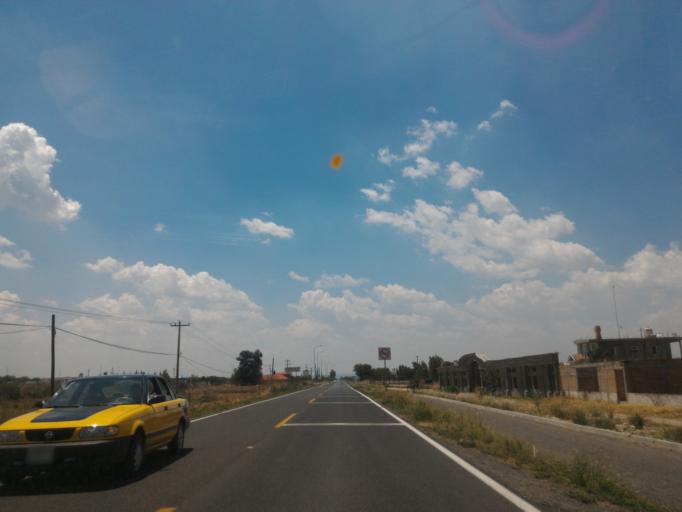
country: MX
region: Guanajuato
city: Ciudad Manuel Doblado
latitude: 20.7538
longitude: -101.9638
